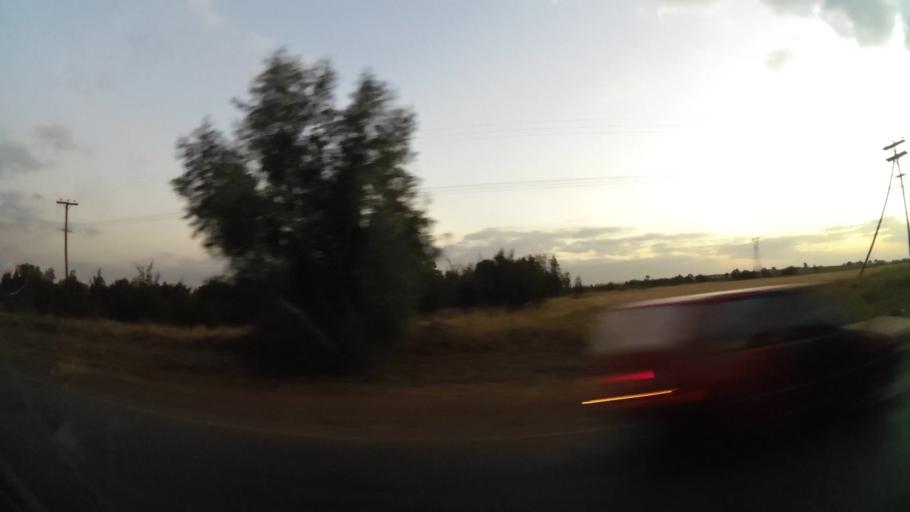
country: ZA
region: Gauteng
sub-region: West Rand District Municipality
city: Randfontein
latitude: -26.0992
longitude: 27.6874
